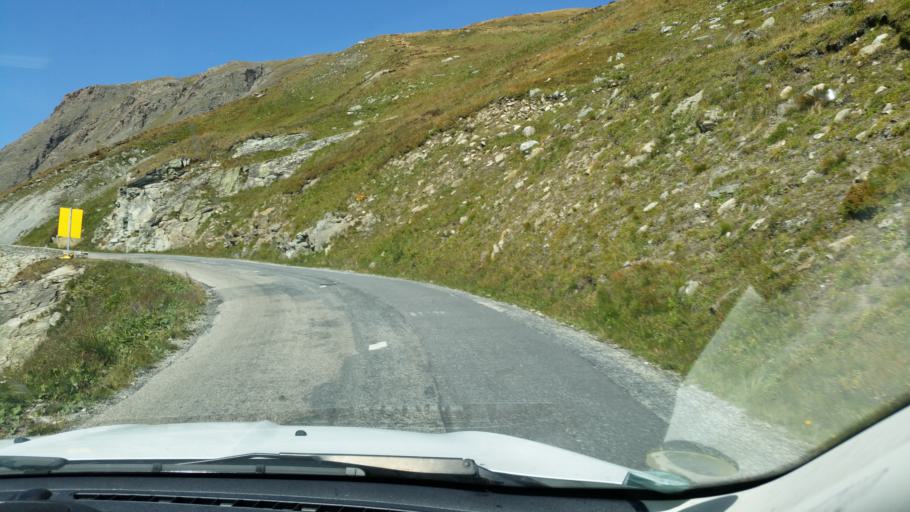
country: FR
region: Rhone-Alpes
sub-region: Departement de la Savoie
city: Val-d'Isere
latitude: 45.3942
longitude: 7.0440
